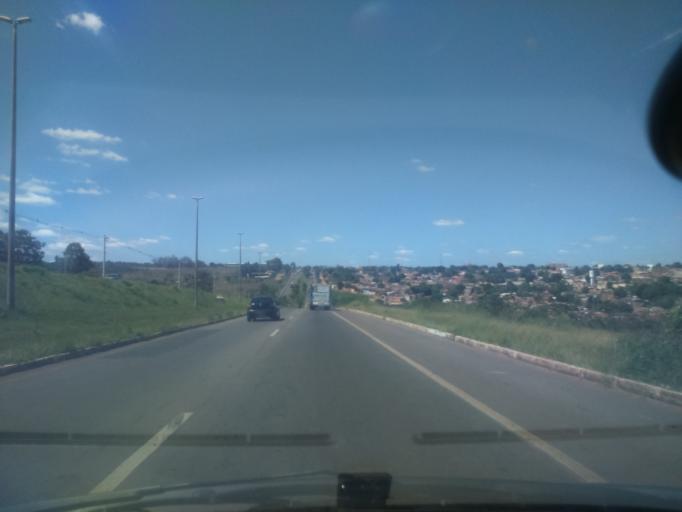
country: BR
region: Goias
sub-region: Luziania
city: Luziania
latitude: -16.0492
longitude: -48.0215
